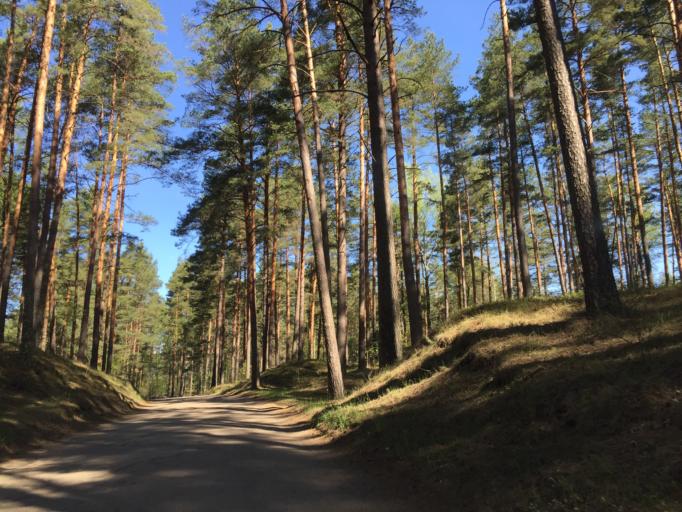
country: LV
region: Adazi
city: Adazi
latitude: 57.0899
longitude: 24.3409
